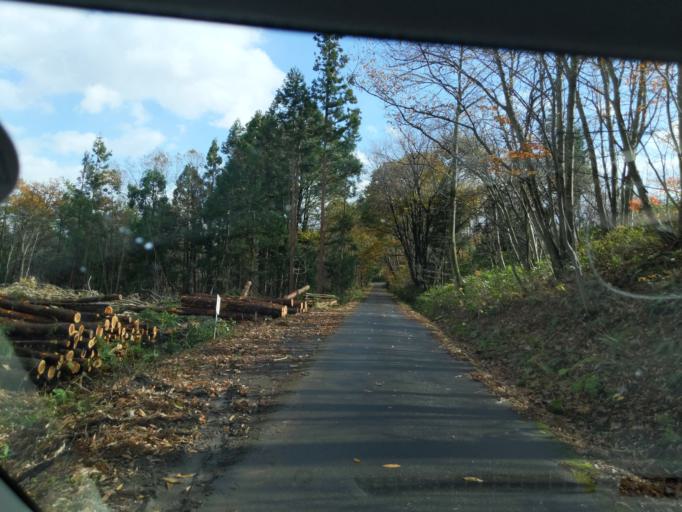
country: JP
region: Iwate
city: Mizusawa
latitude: 39.1021
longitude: 140.9843
